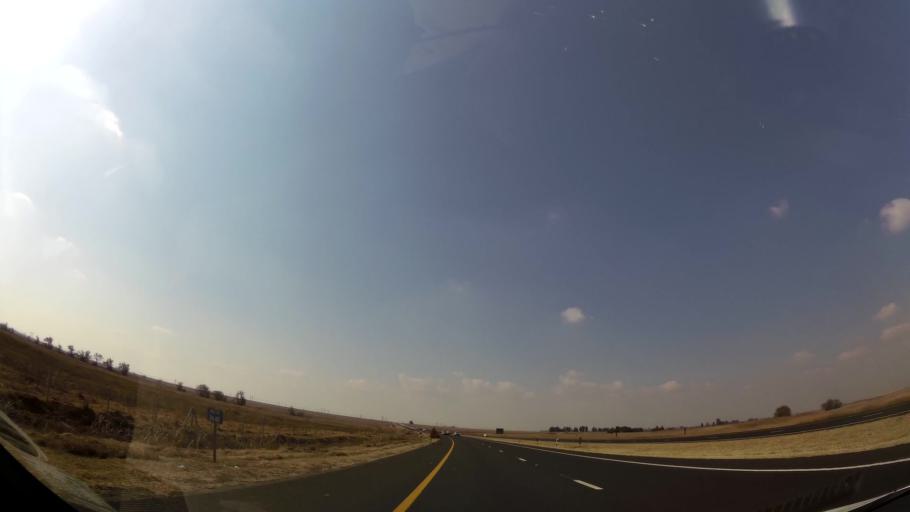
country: ZA
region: Gauteng
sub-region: Ekurhuleni Metropolitan Municipality
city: Springs
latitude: -26.1650
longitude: 28.4564
